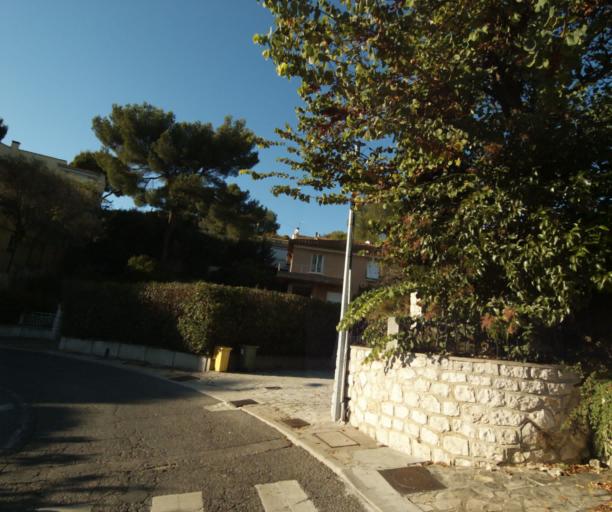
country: FR
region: Provence-Alpes-Cote d'Azur
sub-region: Departement des Bouches-du-Rhone
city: Cassis
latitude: 43.2208
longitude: 5.5408
